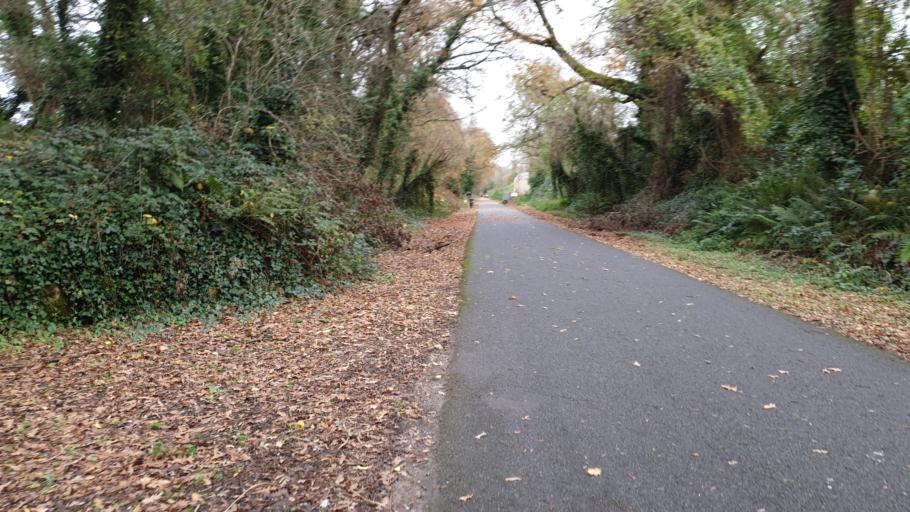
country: IE
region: Munster
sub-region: County Cork
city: Passage West
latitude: 51.8842
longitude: -8.4051
